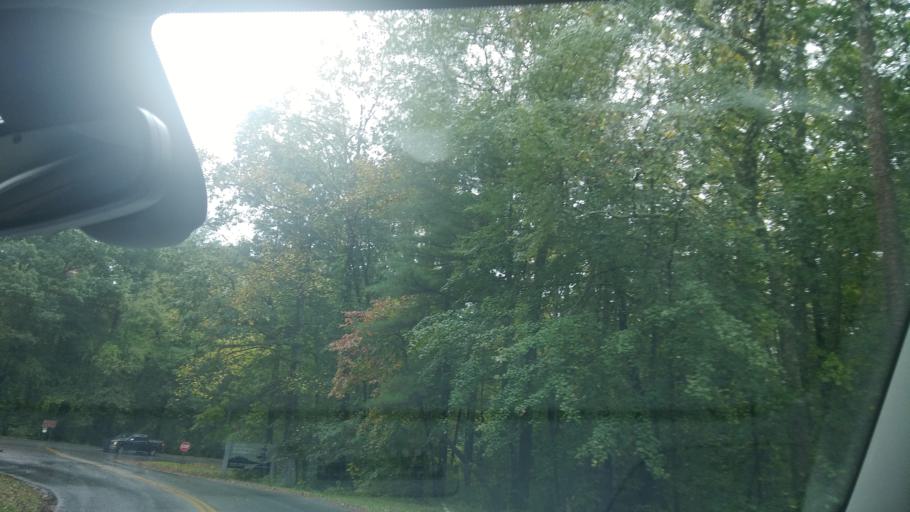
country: US
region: North Carolina
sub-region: Buncombe County
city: Biltmore Forest
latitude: 35.5187
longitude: -82.5304
